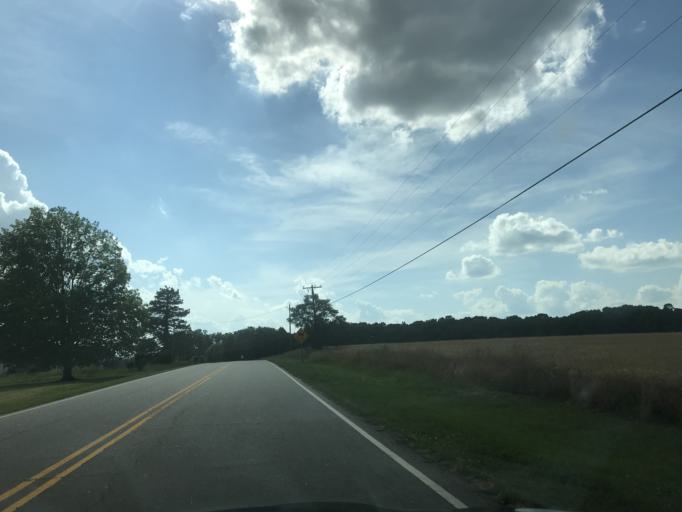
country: US
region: North Carolina
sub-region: Nash County
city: Nashville
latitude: 35.9715
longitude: -78.0118
